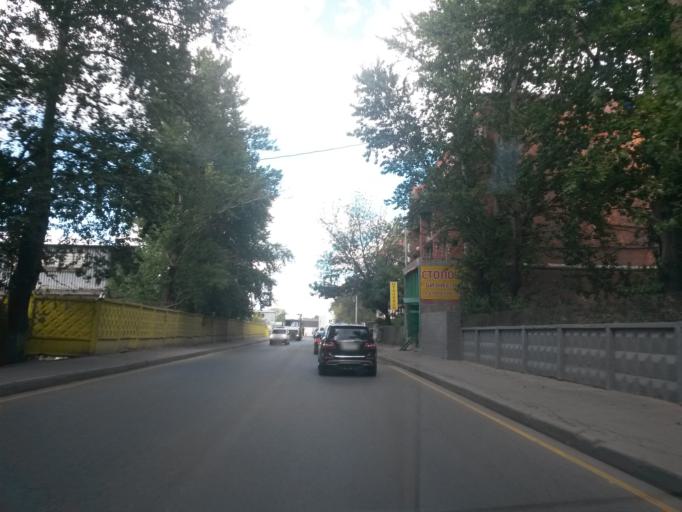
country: RU
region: Moscow
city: Tekstil'shchiki
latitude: 55.7025
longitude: 37.7081
